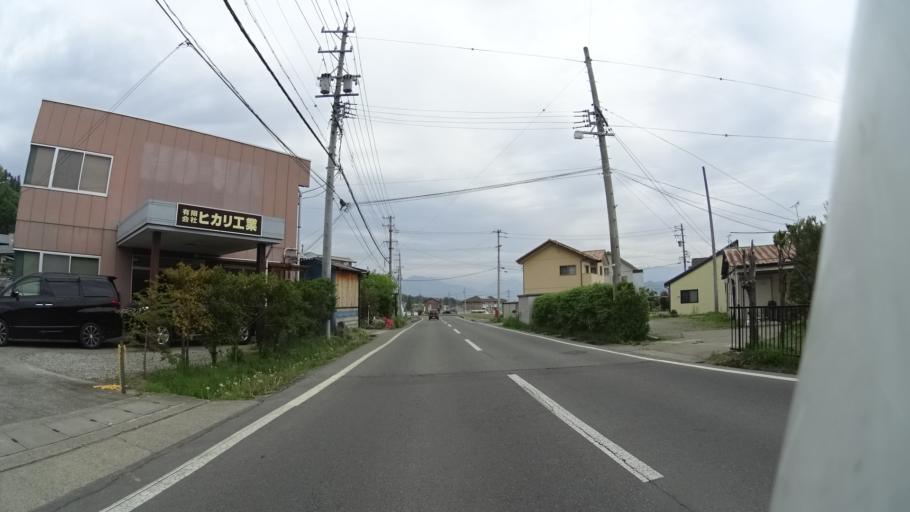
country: JP
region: Nagano
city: Kamimaruko
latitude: 36.3592
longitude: 138.1729
